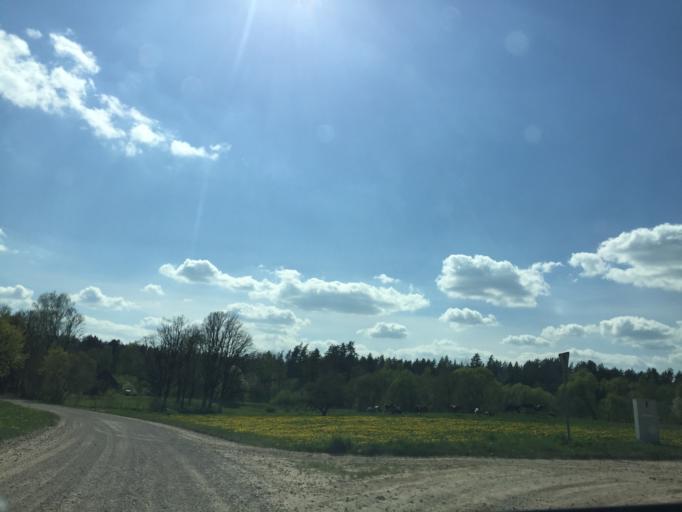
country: LV
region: Vecumnieki
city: Vecumnieki
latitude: 56.4864
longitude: 24.5378
